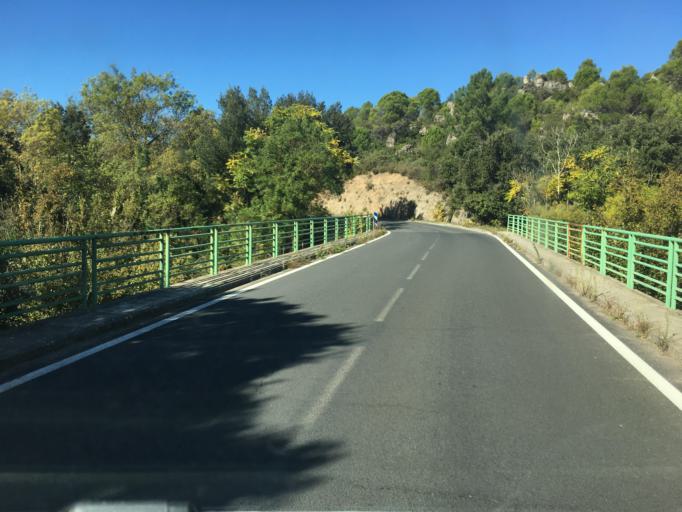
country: FR
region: Languedoc-Roussillon
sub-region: Departement de l'Herault
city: Nebian
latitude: 43.6171
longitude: 3.3632
